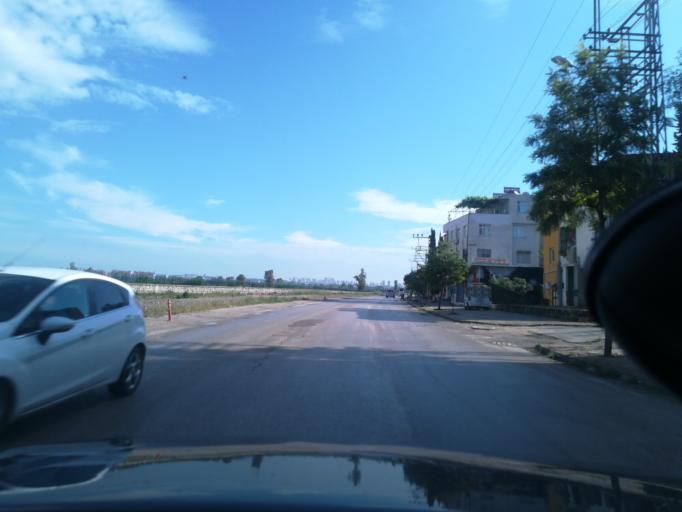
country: TR
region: Adana
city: Adana
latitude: 37.0101
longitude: 35.3578
